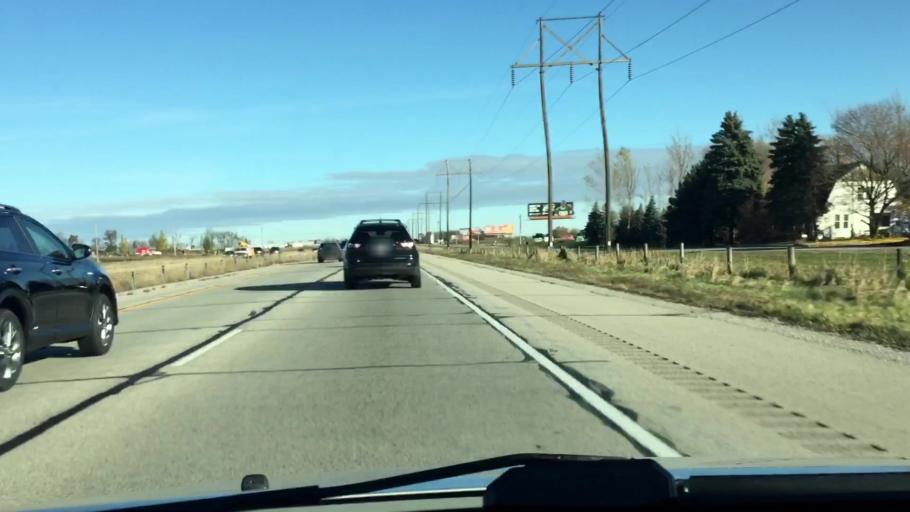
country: US
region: Wisconsin
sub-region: Winnebago County
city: Oshkosh
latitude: 43.9279
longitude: -88.5833
